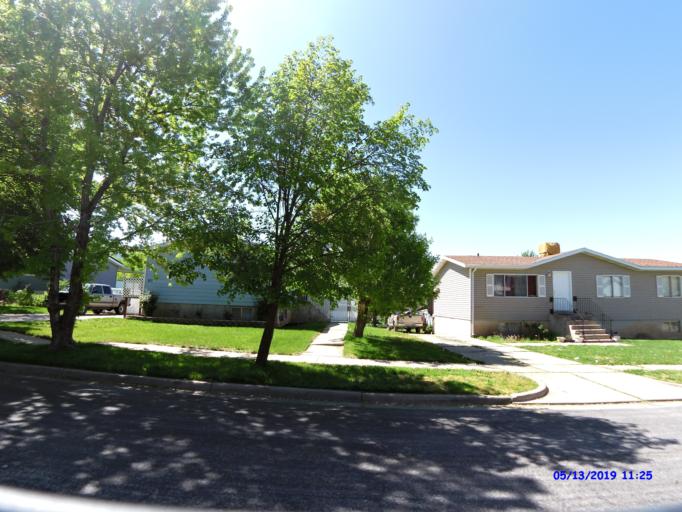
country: US
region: Utah
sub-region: Weber County
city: North Ogden
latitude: 41.2779
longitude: -111.9555
